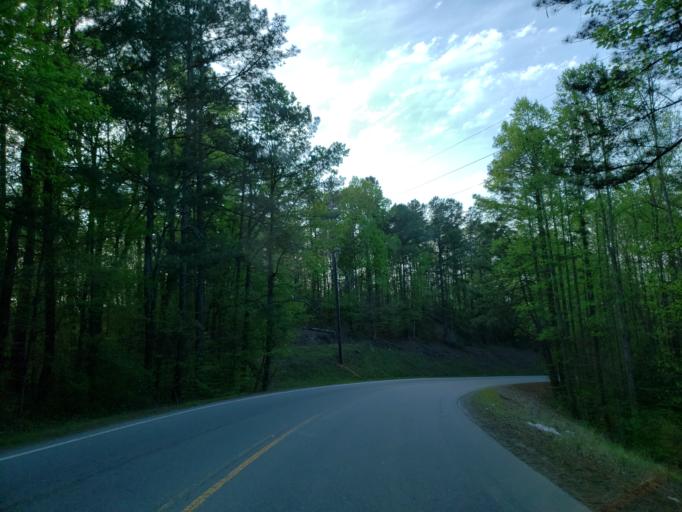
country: US
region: Georgia
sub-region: Cherokee County
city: Ball Ground
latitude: 34.2949
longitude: -84.3946
